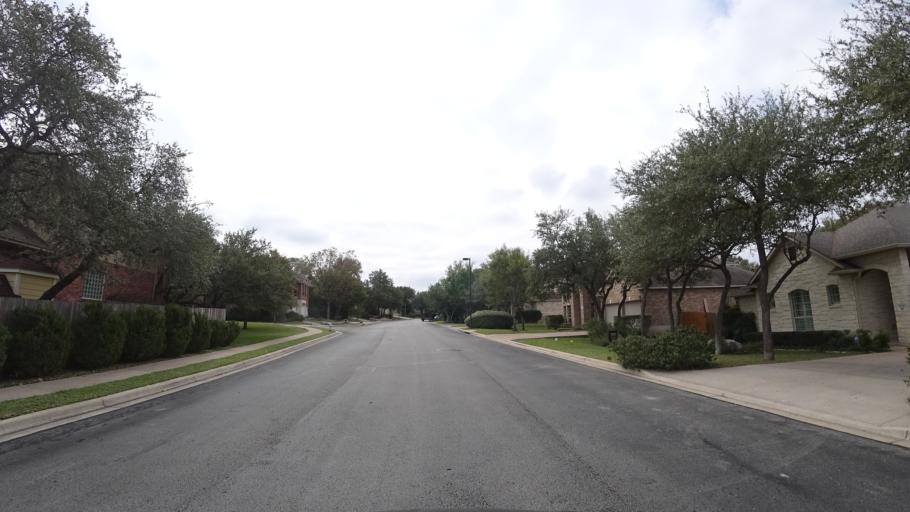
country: US
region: Texas
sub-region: Travis County
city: Shady Hollow
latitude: 30.1897
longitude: -97.9037
